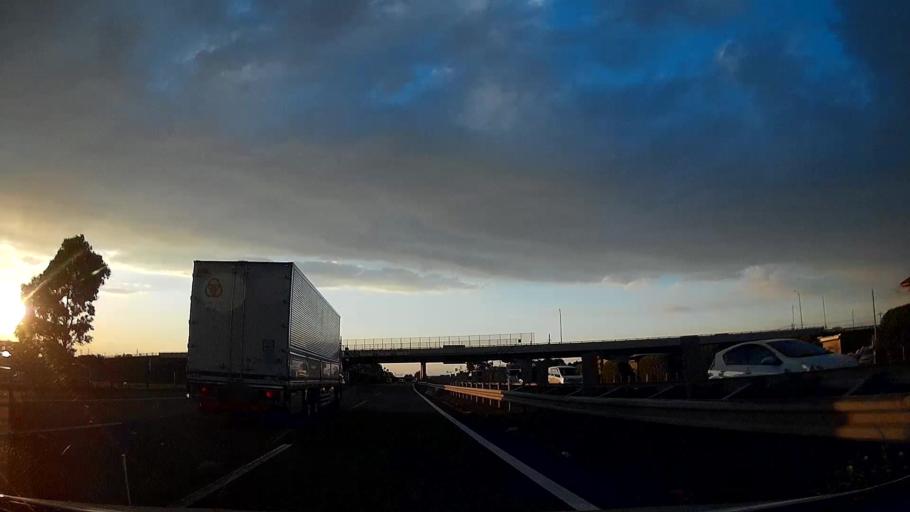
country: JP
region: Saitama
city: Kukichuo
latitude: 36.0729
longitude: 139.6448
